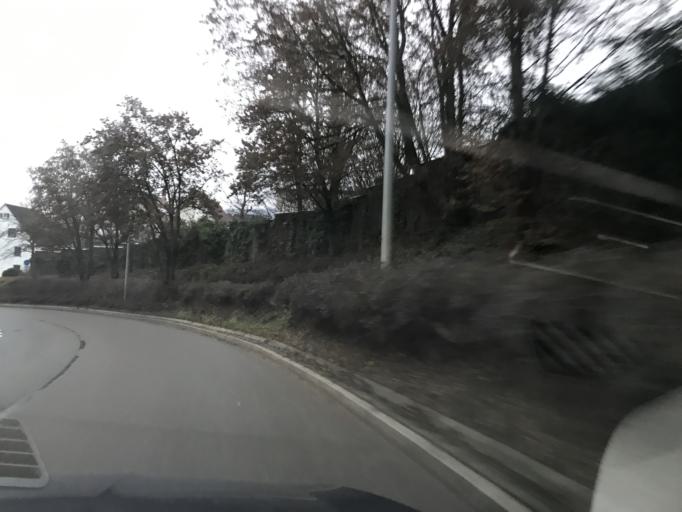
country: DE
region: Baden-Wuerttemberg
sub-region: Regierungsbezirk Stuttgart
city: Plochingen
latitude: 48.7099
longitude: 9.4246
